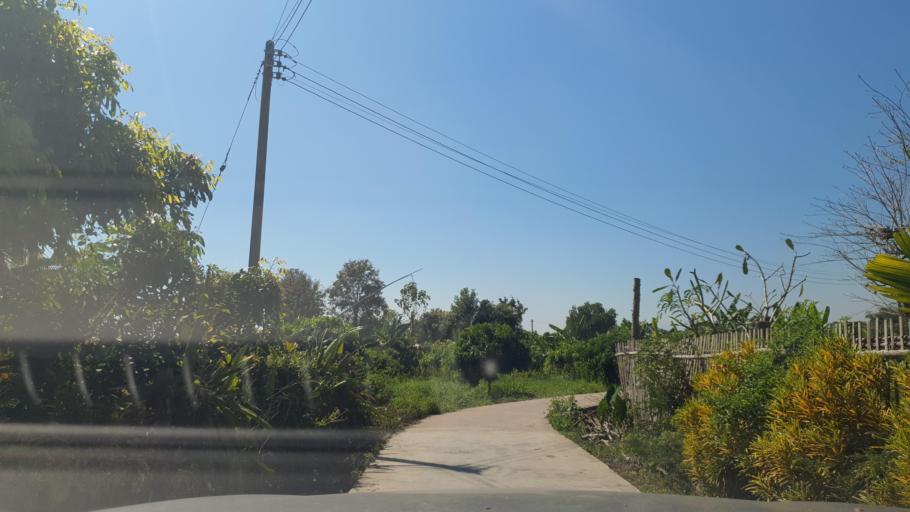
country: TH
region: Chiang Mai
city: San Pa Tong
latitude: 18.6564
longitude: 98.8359
